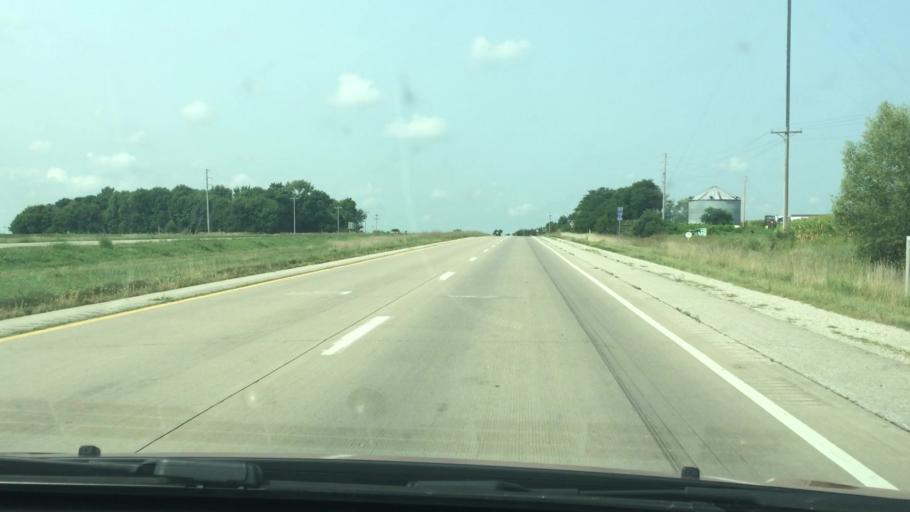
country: US
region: Iowa
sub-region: Cedar County
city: Durant
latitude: 41.5180
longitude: -90.8962
